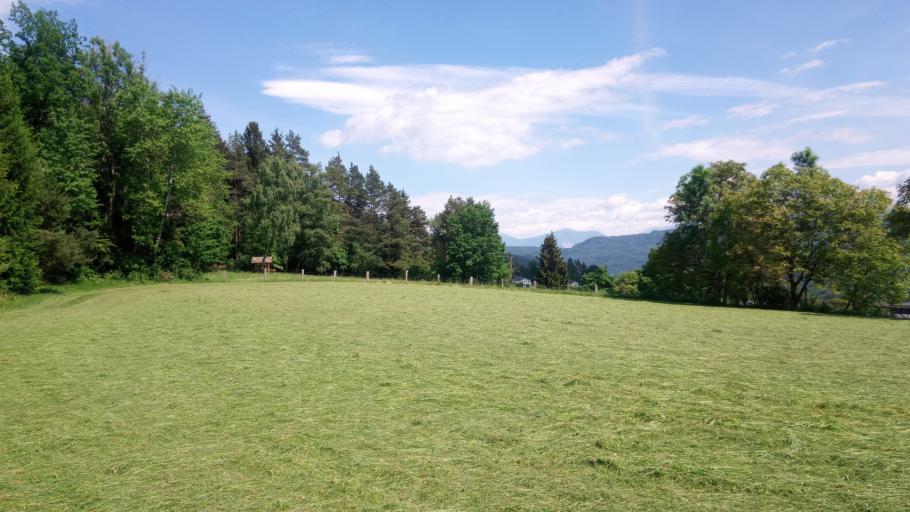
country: AT
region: Carinthia
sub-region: Politischer Bezirk Klagenfurt Land
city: Schiefling am See
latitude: 46.6077
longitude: 14.0967
